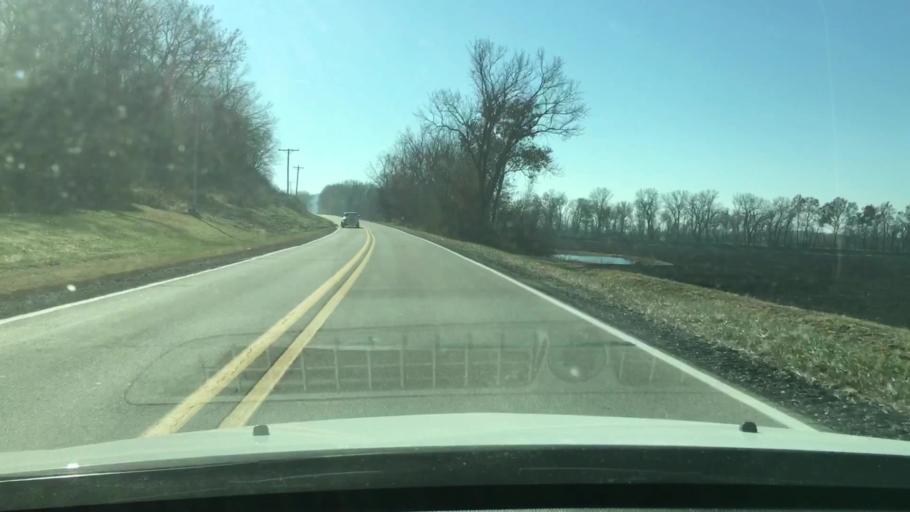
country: US
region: Illinois
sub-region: Morgan County
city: Meredosia
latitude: 39.7220
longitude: -90.5684
